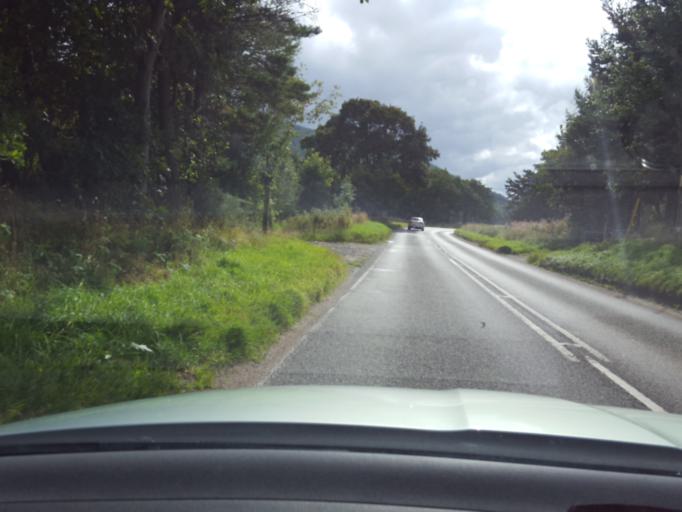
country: GB
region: Scotland
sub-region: Aberdeenshire
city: Ballater
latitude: 57.0619
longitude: -3.0174
